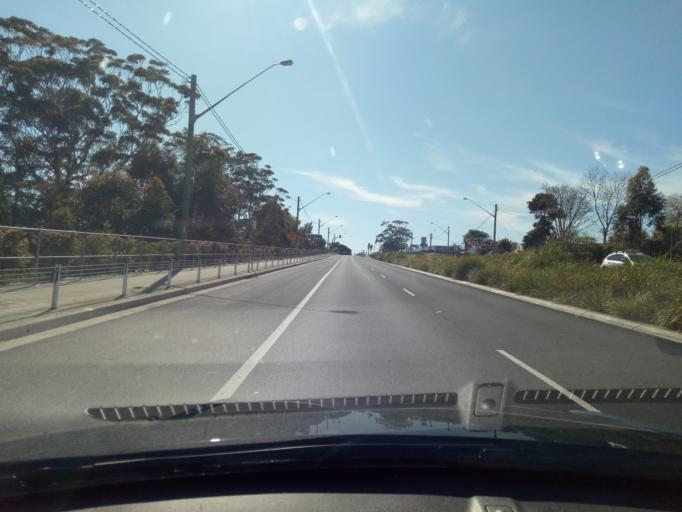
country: AU
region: New South Wales
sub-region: Gosford Shire
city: Holgate
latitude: -33.4233
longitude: 151.4359
